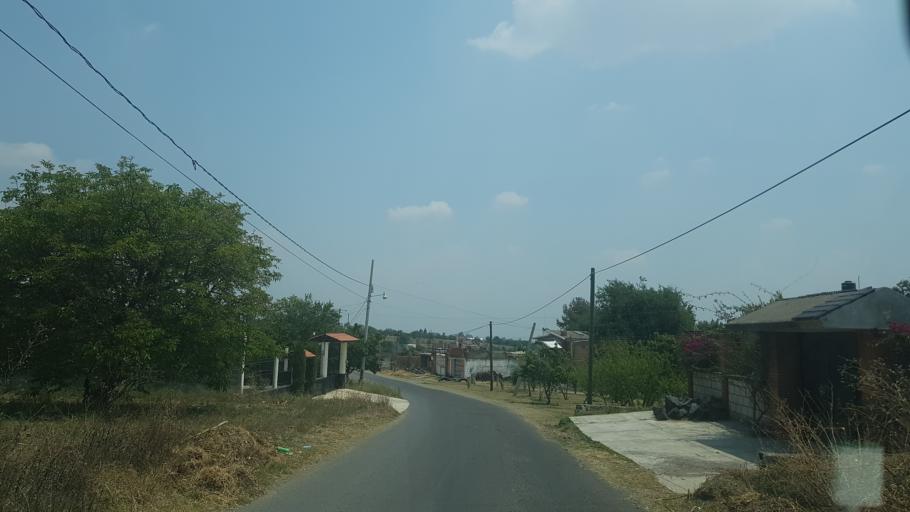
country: MX
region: Puebla
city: San Andres Calpan
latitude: 19.0977
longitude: -98.4776
